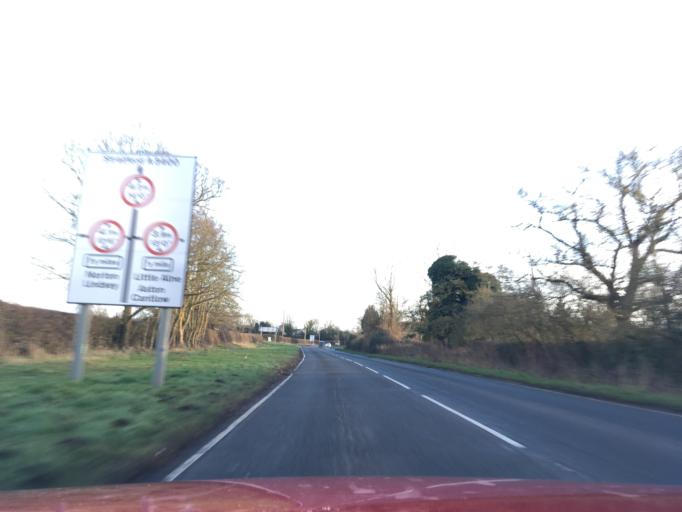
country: GB
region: England
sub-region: Warwickshire
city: Henley in Arden
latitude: 52.2479
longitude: -1.7523
